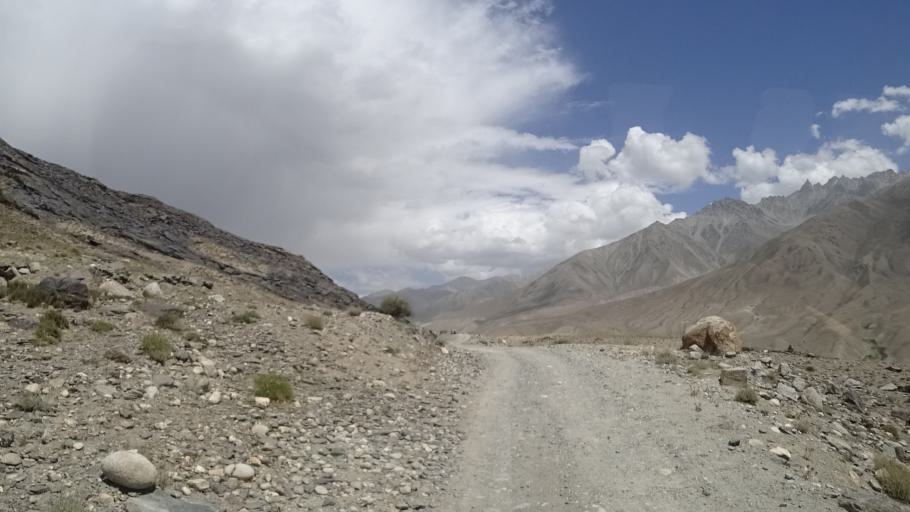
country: AF
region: Badakhshan
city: Khandud
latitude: 37.0962
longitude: 72.7099
